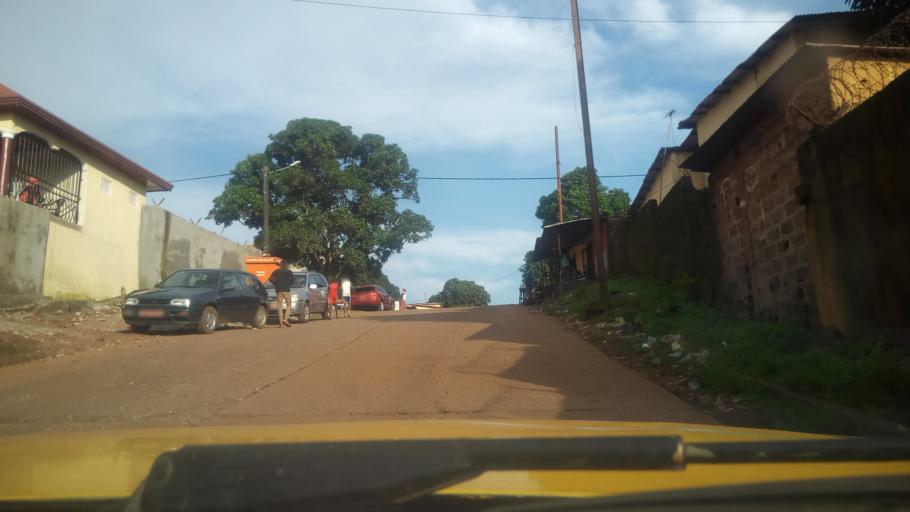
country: GN
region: Conakry
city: Conakry
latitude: 9.6217
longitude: -13.6100
